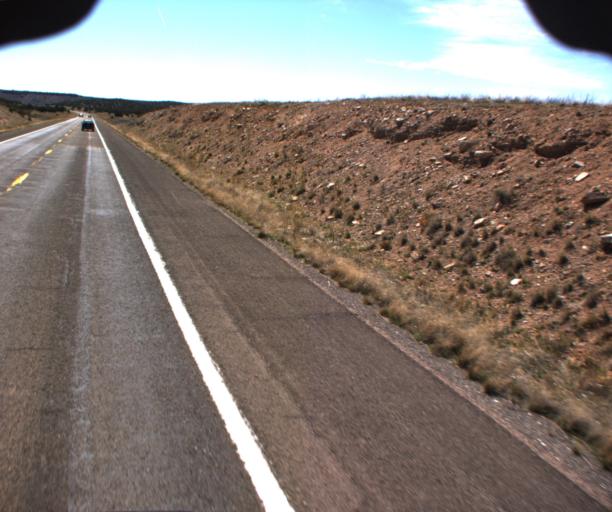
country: US
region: Arizona
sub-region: Mohave County
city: Peach Springs
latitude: 35.4555
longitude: -113.6240
